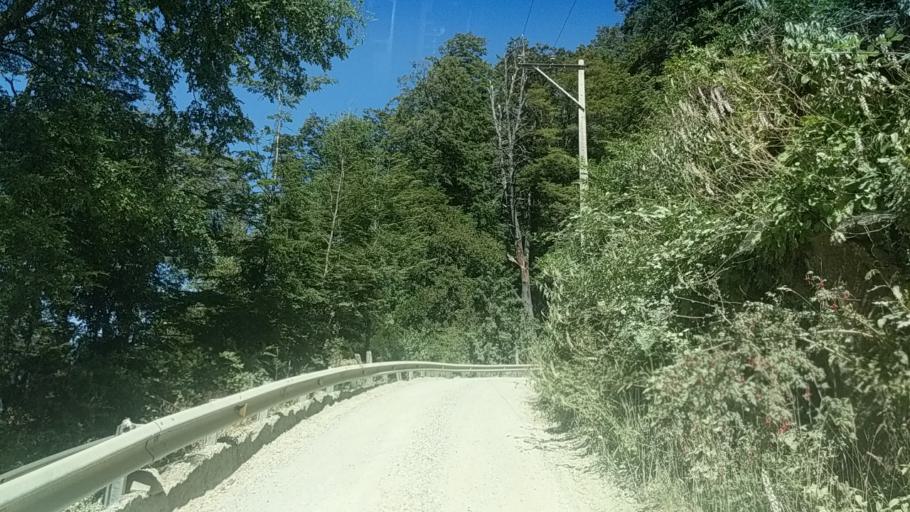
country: CL
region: Araucania
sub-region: Provincia de Cautin
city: Pucon
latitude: -39.0640
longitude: -71.7293
